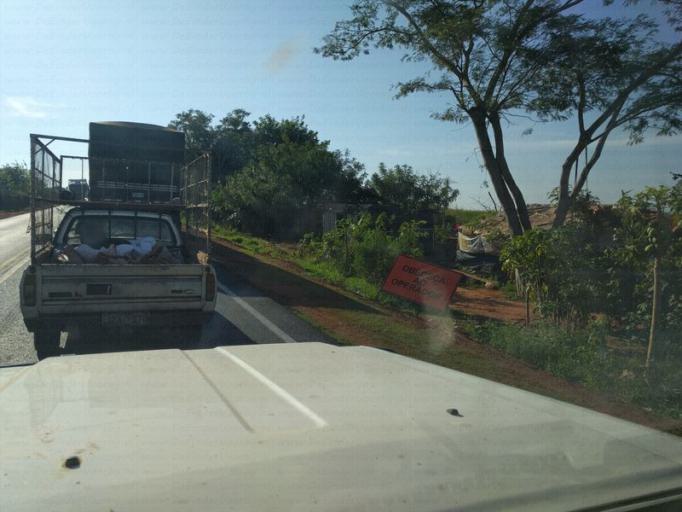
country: BR
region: Mato Grosso do Sul
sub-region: Eldorado
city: Eldorado
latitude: -23.8075
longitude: -54.3178
